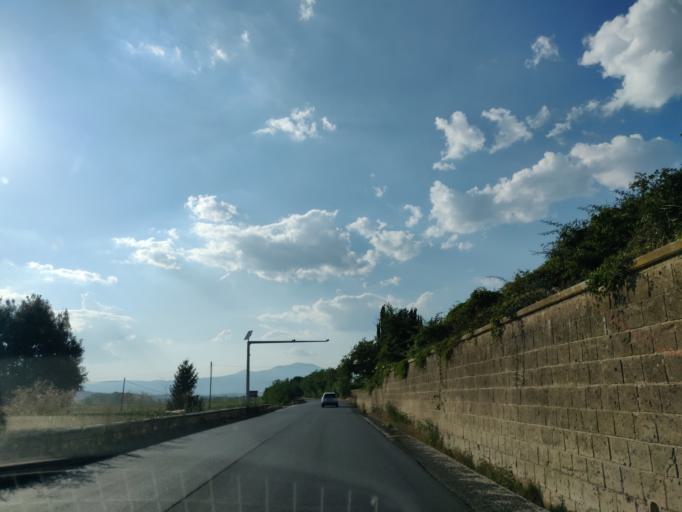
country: IT
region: Latium
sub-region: Provincia di Viterbo
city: Proceno
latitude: 42.7800
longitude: 11.8364
